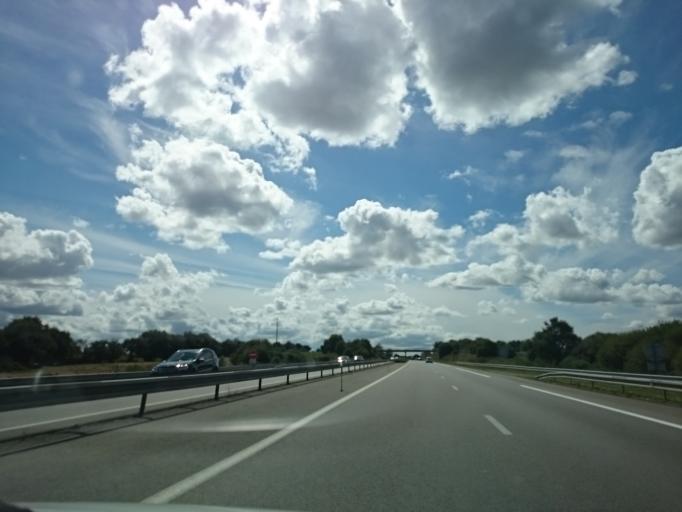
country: FR
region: Pays de la Loire
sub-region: Departement de la Loire-Atlantique
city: Oudon
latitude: 47.3656
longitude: -1.3083
